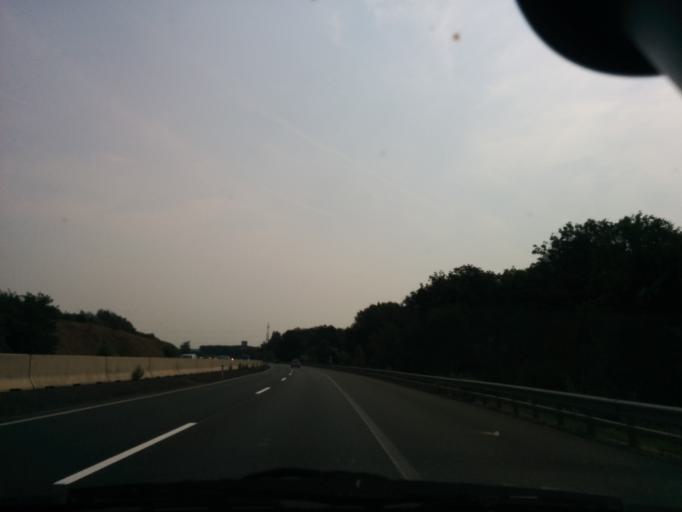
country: AT
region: Lower Austria
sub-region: Politischer Bezirk Korneuburg
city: Stockerau
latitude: 48.3768
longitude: 16.2275
